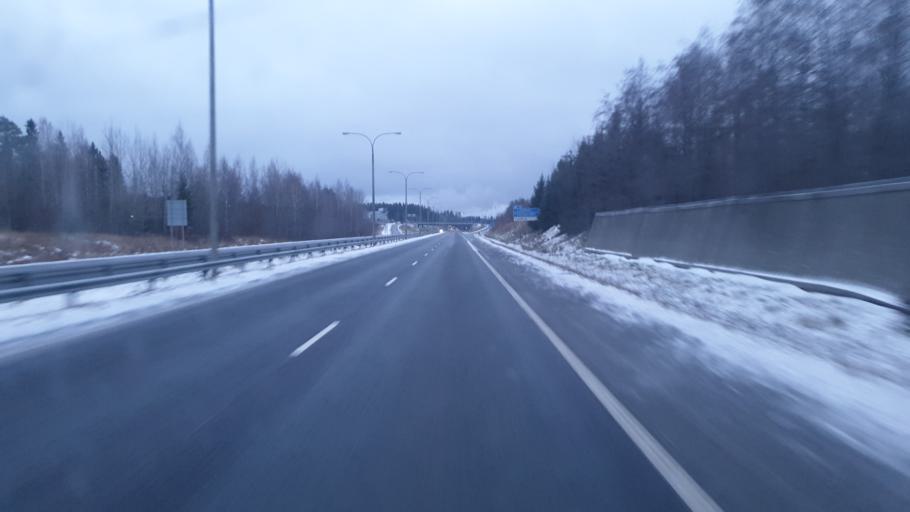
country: FI
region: Northern Savo
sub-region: Kuopio
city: Kuopio
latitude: 62.9784
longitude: 27.7056
